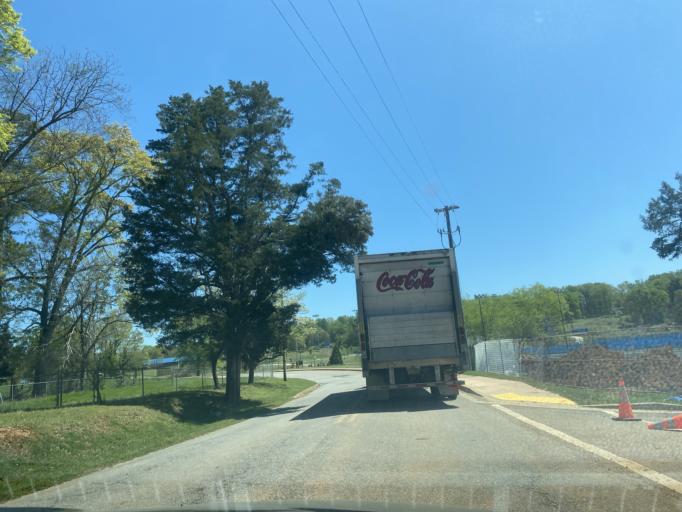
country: US
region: South Carolina
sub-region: Cherokee County
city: Gaffney
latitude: 35.0565
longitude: -81.6475
